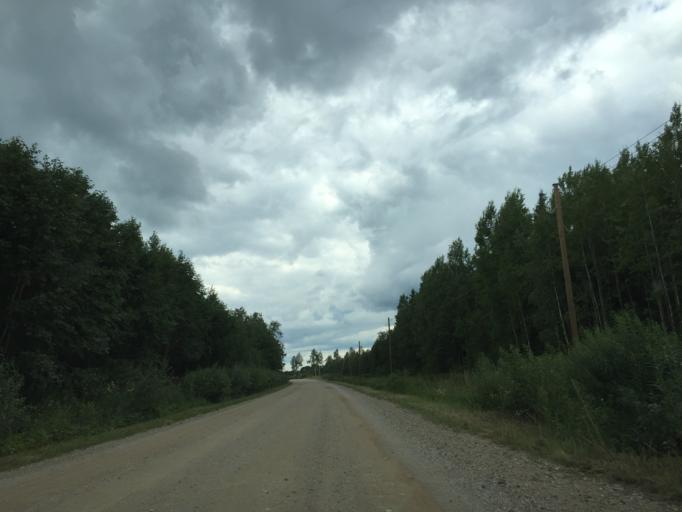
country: LV
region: Malpils
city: Malpils
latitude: 56.8740
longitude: 25.0031
